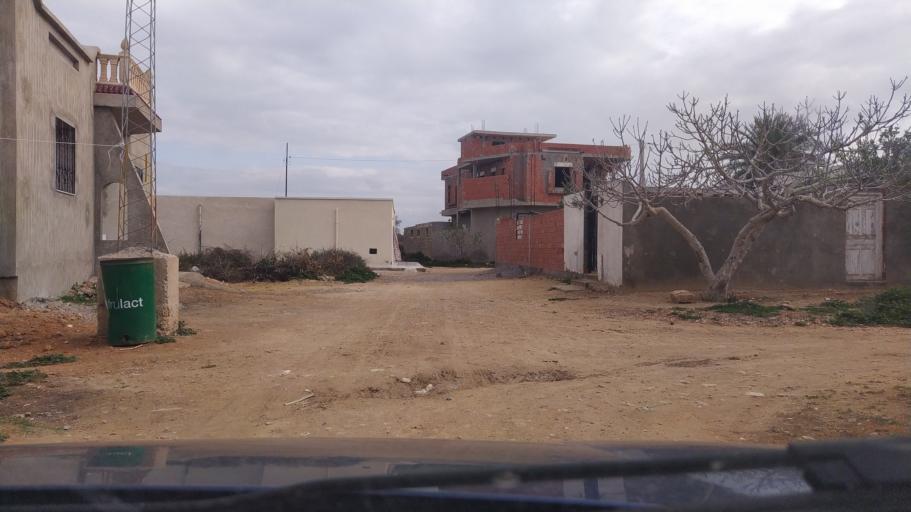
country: TN
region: Al Munastir
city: Sidi Bin Nur
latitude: 35.5188
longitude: 10.9289
